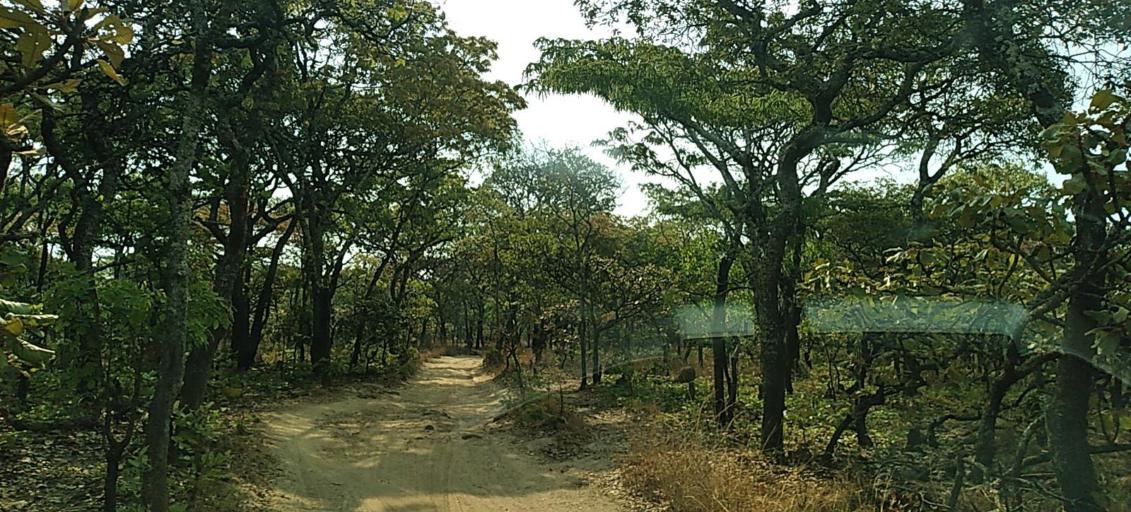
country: ZM
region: North-Western
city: Solwezi
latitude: -12.0732
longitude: 26.2323
